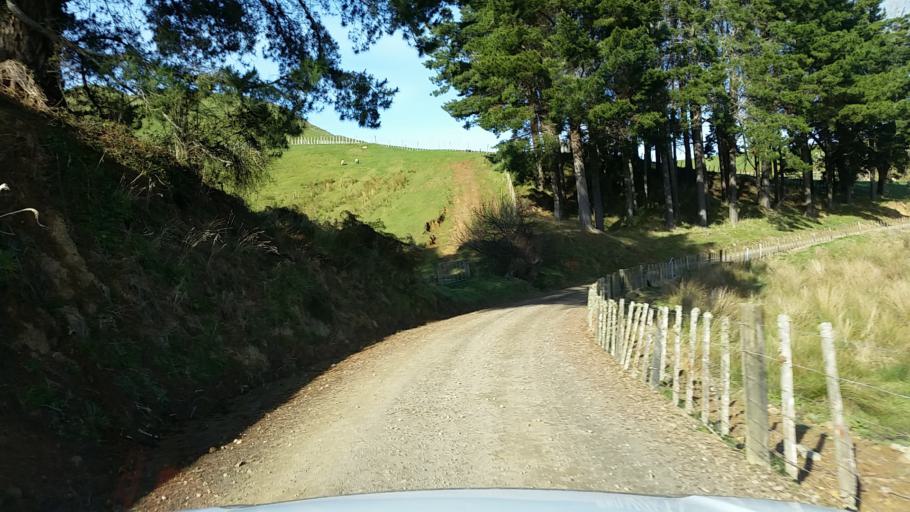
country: NZ
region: Taranaki
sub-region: South Taranaki District
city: Eltham
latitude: -39.3179
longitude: 174.5327
